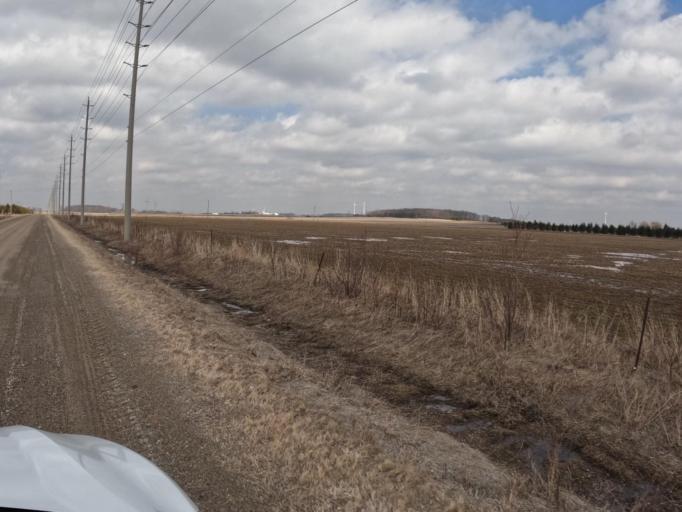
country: CA
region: Ontario
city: Shelburne
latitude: 44.0431
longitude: -80.3181
